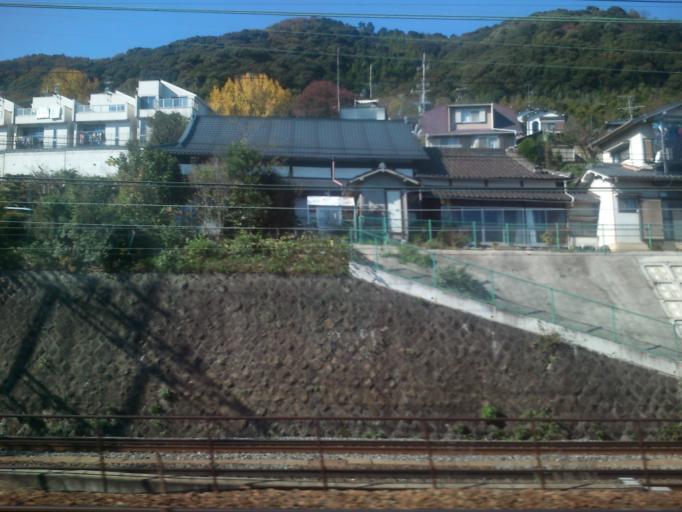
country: JP
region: Kyoto
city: Yawata
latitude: 34.8985
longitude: 135.6845
